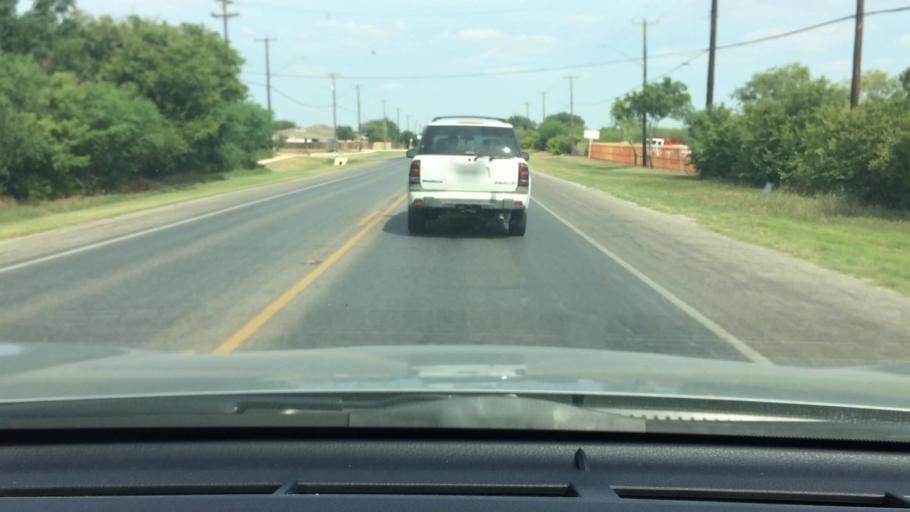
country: US
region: Texas
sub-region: Bexar County
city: San Antonio
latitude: 29.3317
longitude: -98.4461
